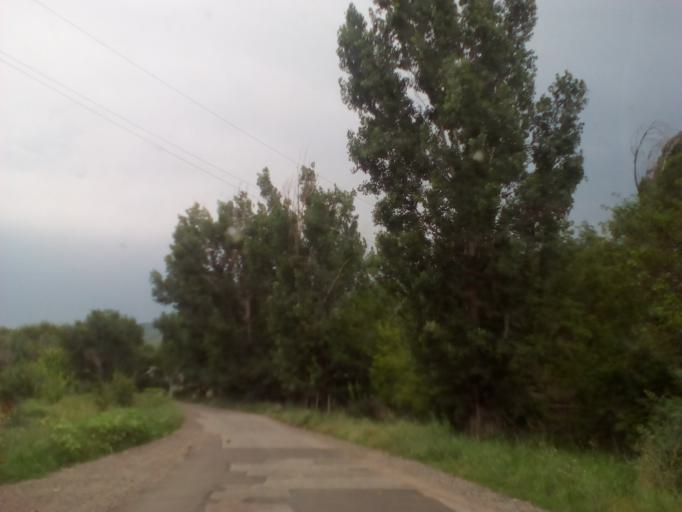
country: KZ
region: Almaty Oblysy
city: Burunday
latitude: 43.1599
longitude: 76.3880
